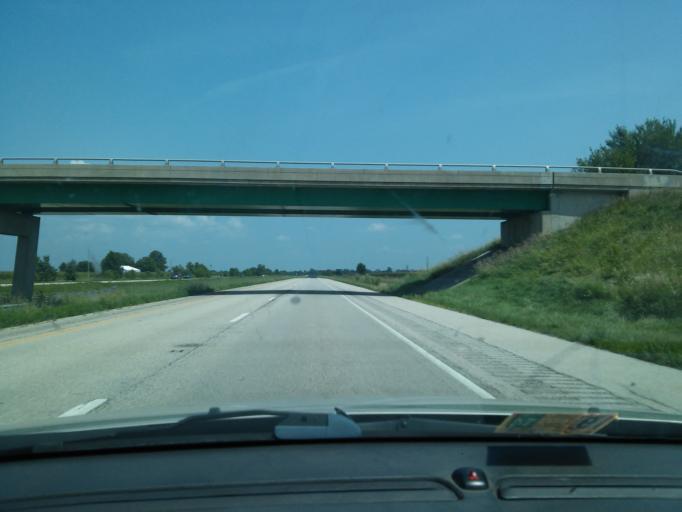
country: US
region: Illinois
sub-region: Sangamon County
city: New Berlin
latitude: 39.7409
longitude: -89.8445
